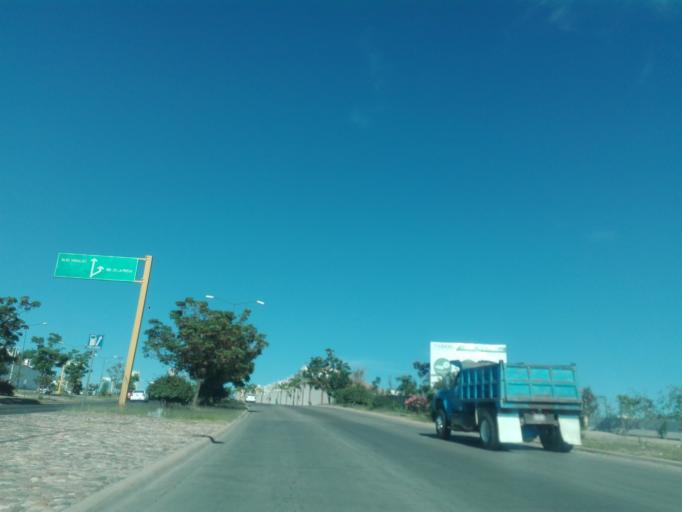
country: MX
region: Guanajuato
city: Leon
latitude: 21.1708
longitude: -101.6777
